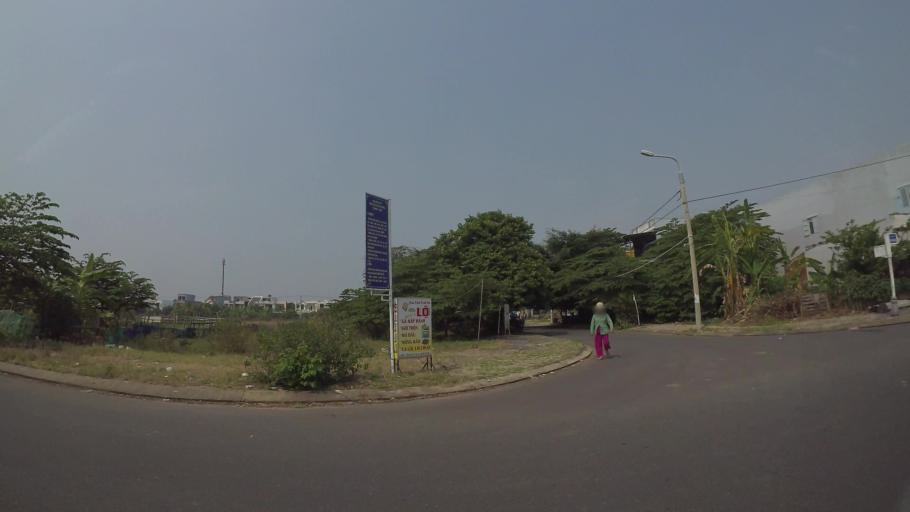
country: VN
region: Da Nang
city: Cam Le
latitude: 15.9813
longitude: 108.2141
